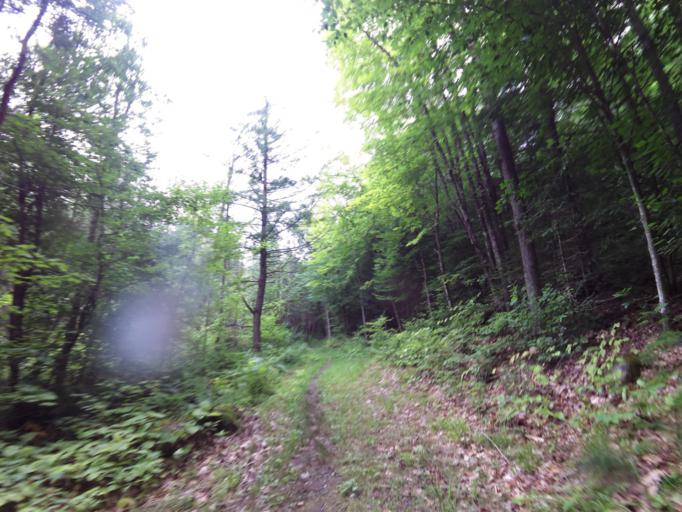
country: CA
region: Quebec
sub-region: Outaouais
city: Wakefield
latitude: 45.6124
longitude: -76.0469
